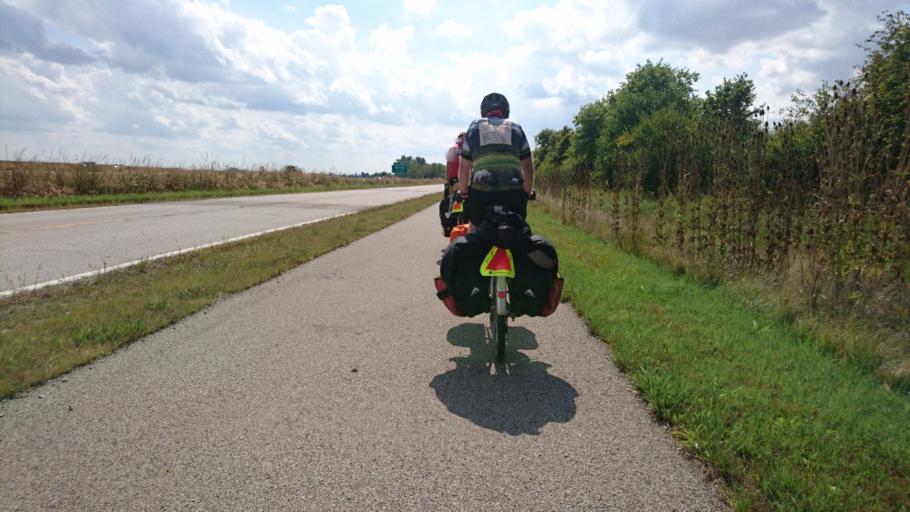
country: US
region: Illinois
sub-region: McLean County
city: Twin Grove
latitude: 40.4199
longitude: -89.0466
